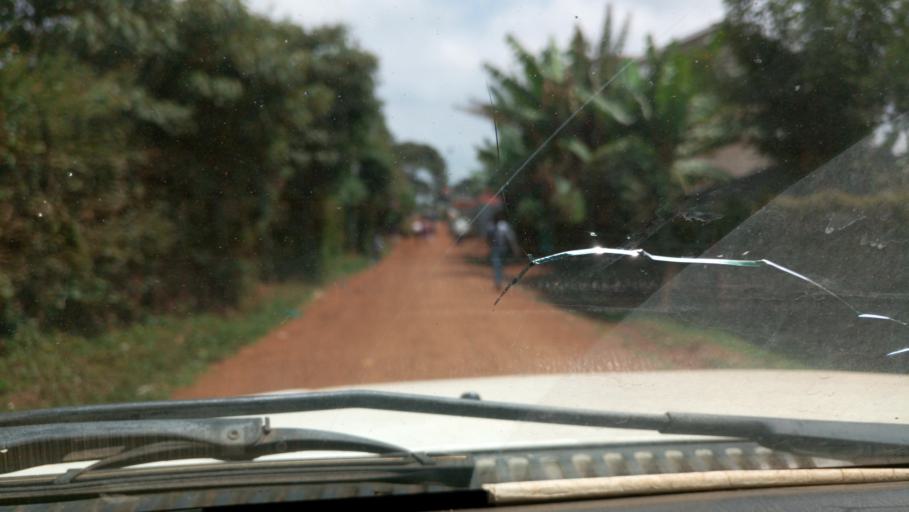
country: KE
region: Kiambu
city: Kikuyu
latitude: -1.2838
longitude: 36.7180
